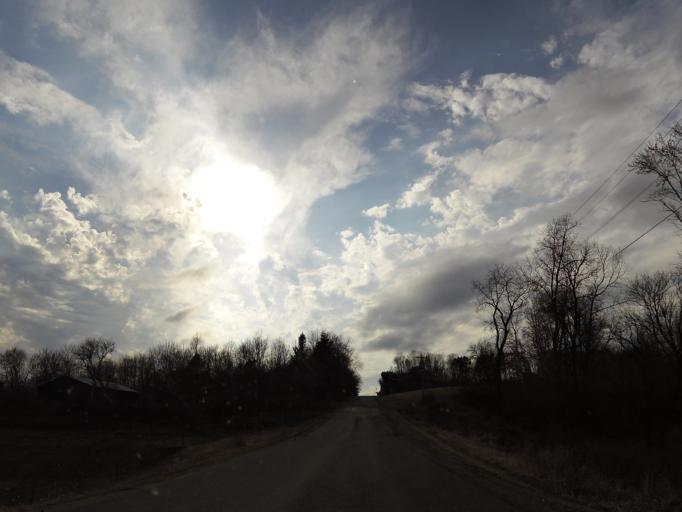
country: US
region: Wisconsin
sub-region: Pierce County
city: Ellsworth
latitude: 44.7503
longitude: -92.4738
